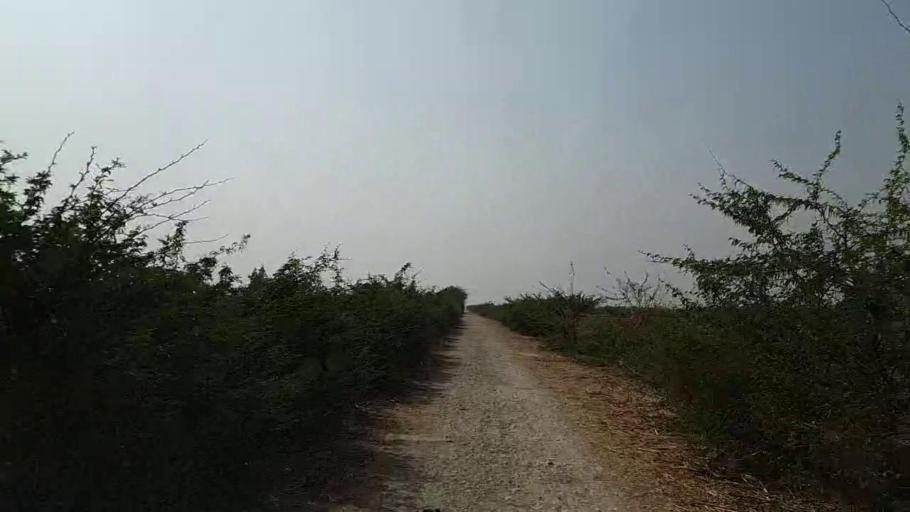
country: PK
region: Sindh
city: Naukot
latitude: 24.7605
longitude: 69.3397
